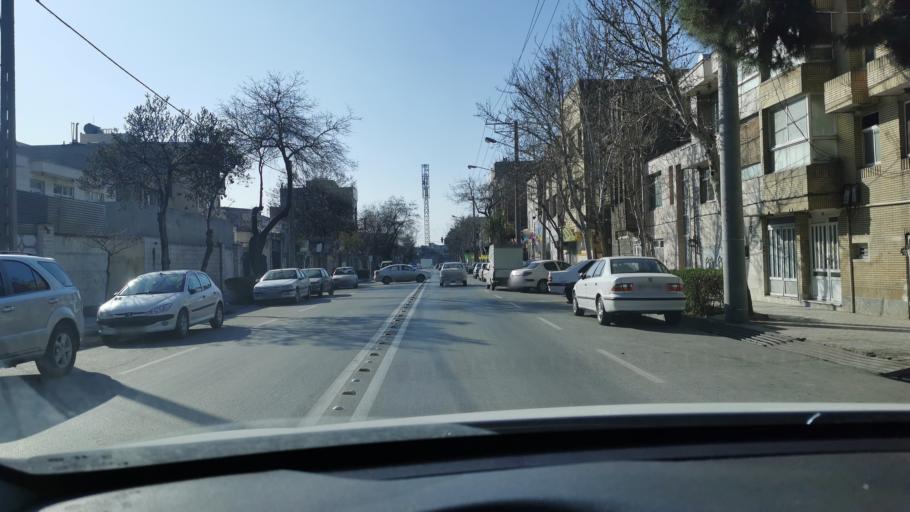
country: IR
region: Razavi Khorasan
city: Mashhad
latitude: 36.2777
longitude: 59.5750
